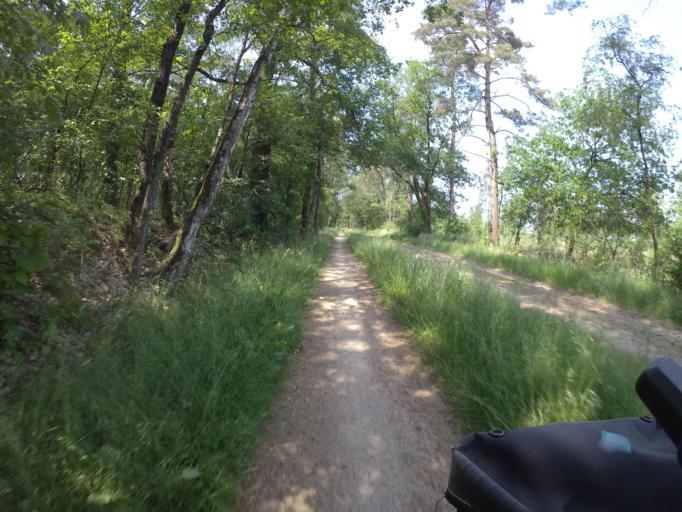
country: NL
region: Overijssel
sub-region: Gemeente Hof van Twente
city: Markelo
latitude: 52.2675
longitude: 6.5043
